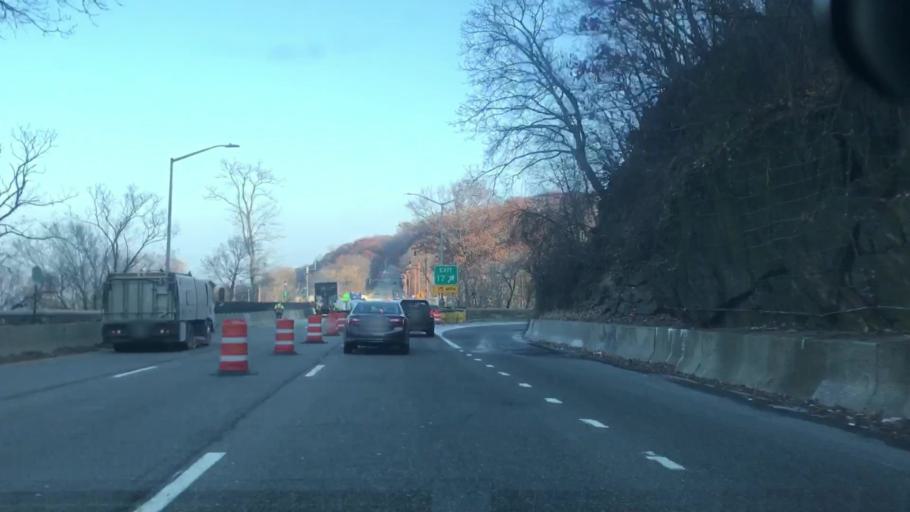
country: US
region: New York
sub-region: New York County
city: Inwood
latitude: 40.8663
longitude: -73.9322
